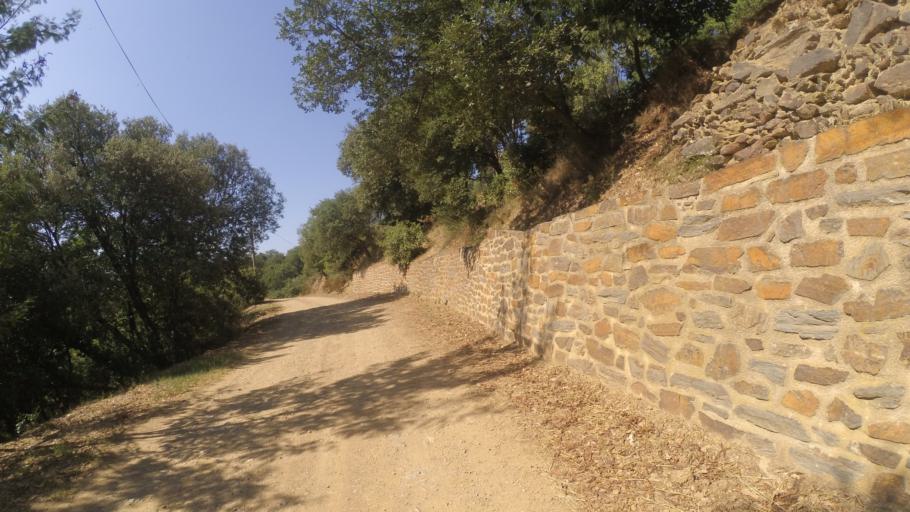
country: FR
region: Languedoc-Roussillon
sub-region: Departement des Pyrenees-Orientales
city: Millas
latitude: 42.6192
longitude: 2.6773
